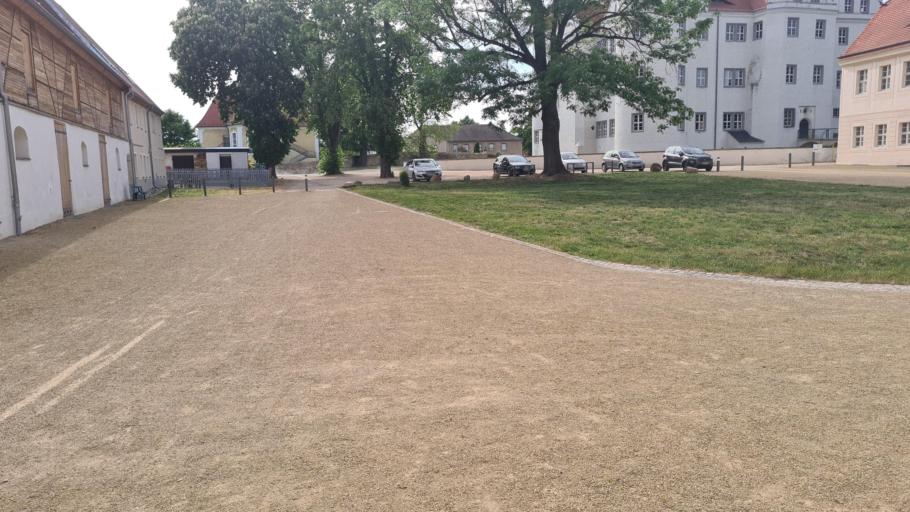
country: DE
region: Brandenburg
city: Grosskmehlen
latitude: 51.3794
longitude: 13.7260
